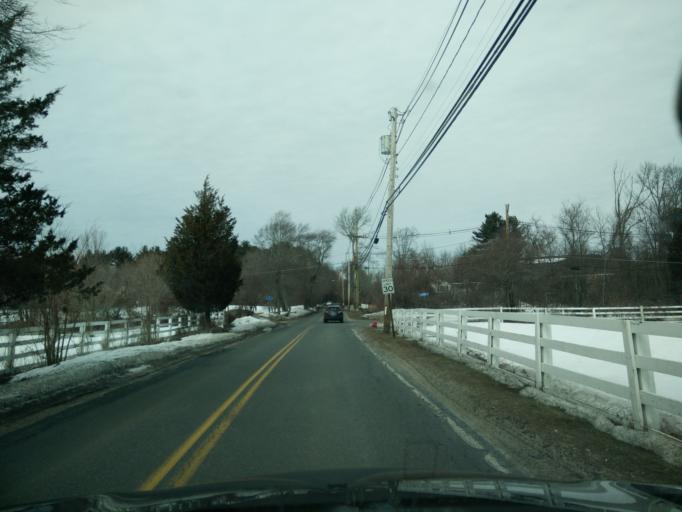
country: US
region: Massachusetts
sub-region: Norfolk County
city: Westwood
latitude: 42.1858
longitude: -71.2468
